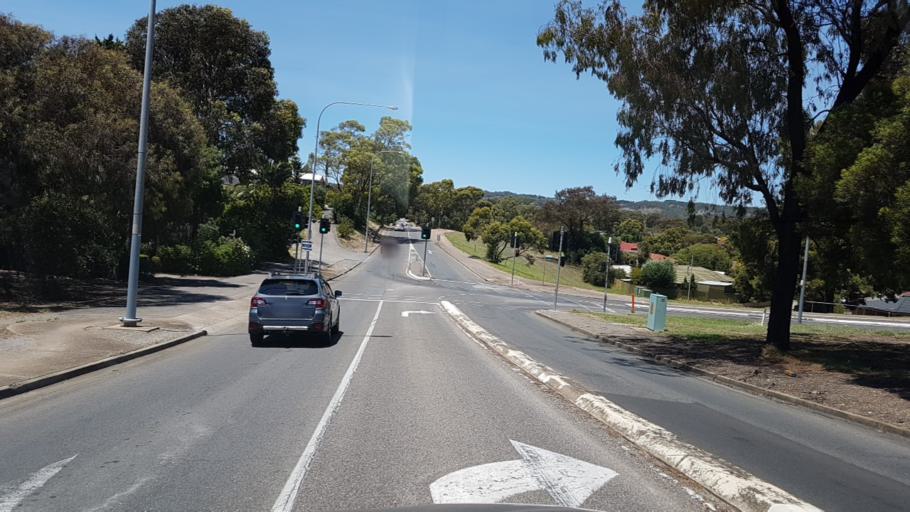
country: AU
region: South Australia
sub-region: Marion
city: Trott Park
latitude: -35.0826
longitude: 138.5581
